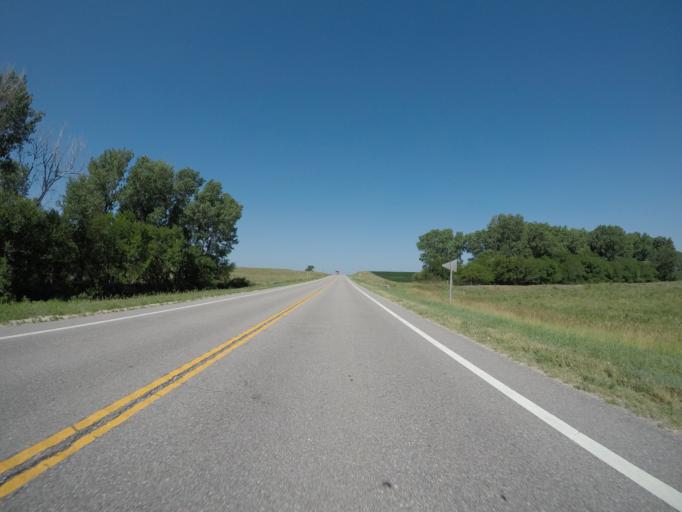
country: US
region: Kansas
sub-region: Cloud County
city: Concordia
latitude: 39.3645
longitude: -97.4478
